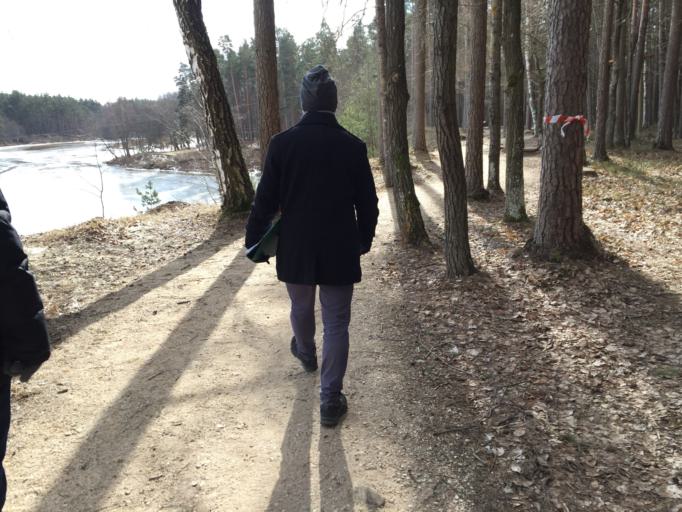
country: LV
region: Valmieras Rajons
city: Valmiera
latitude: 57.5397
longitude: 25.4433
